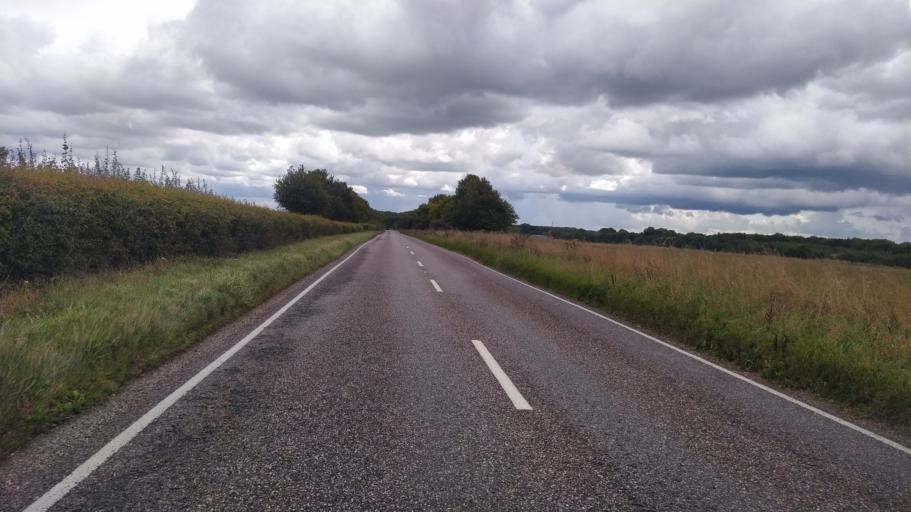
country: GB
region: England
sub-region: Wiltshire
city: Bower Chalke
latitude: 50.9441
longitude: -1.9760
